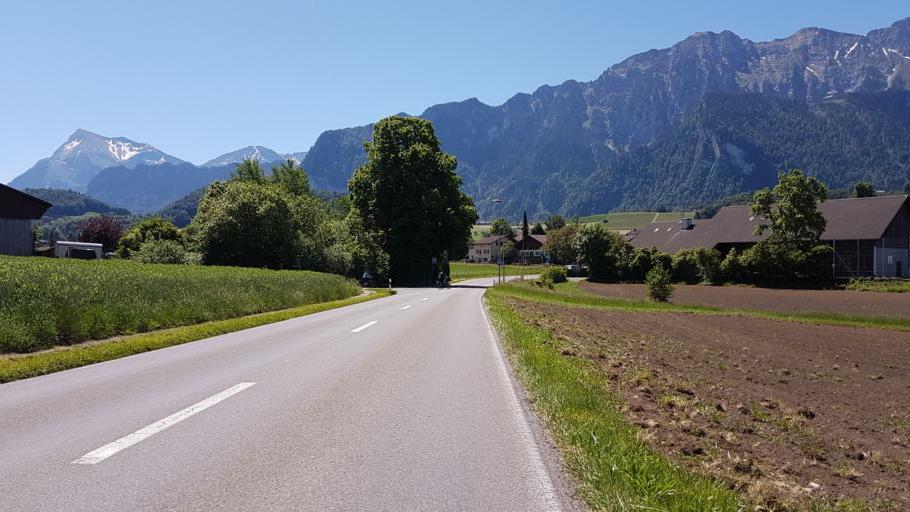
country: CH
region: Bern
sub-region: Thun District
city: Thierachern
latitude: 46.7297
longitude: 7.5845
